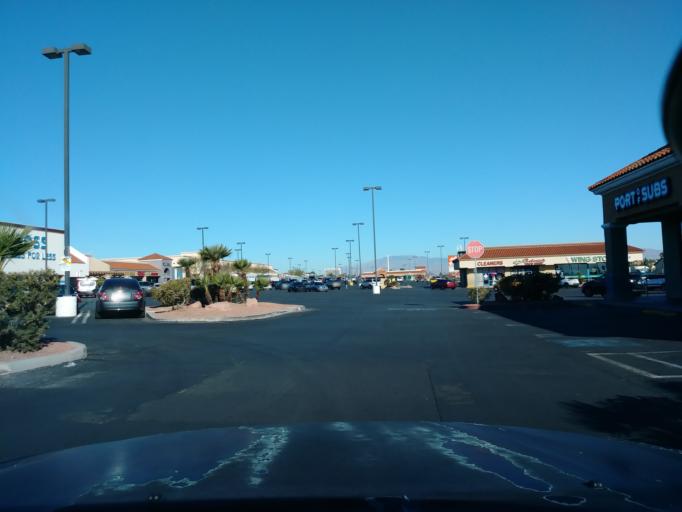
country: US
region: Nevada
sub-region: Clark County
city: Spring Valley
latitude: 36.1606
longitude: -115.2446
